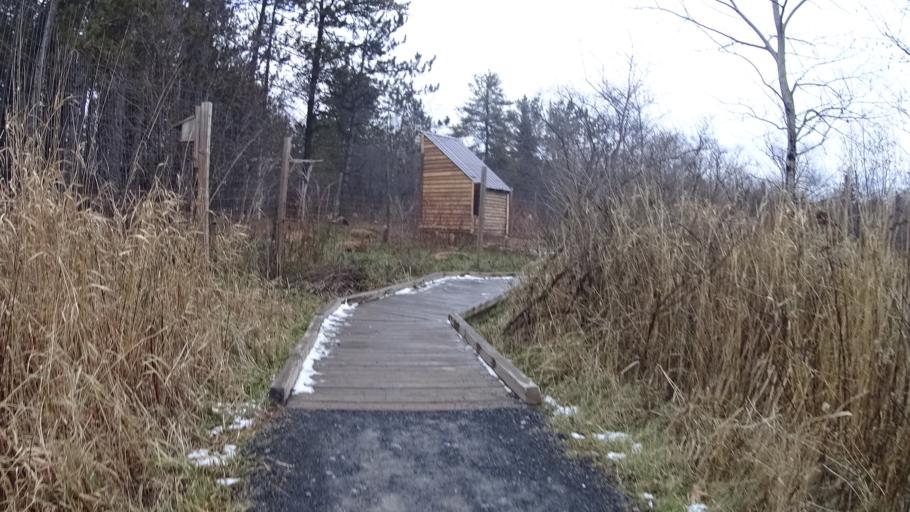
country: US
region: Minnesota
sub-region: Saint Louis County
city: Arnold
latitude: 46.8378
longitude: -92.0843
